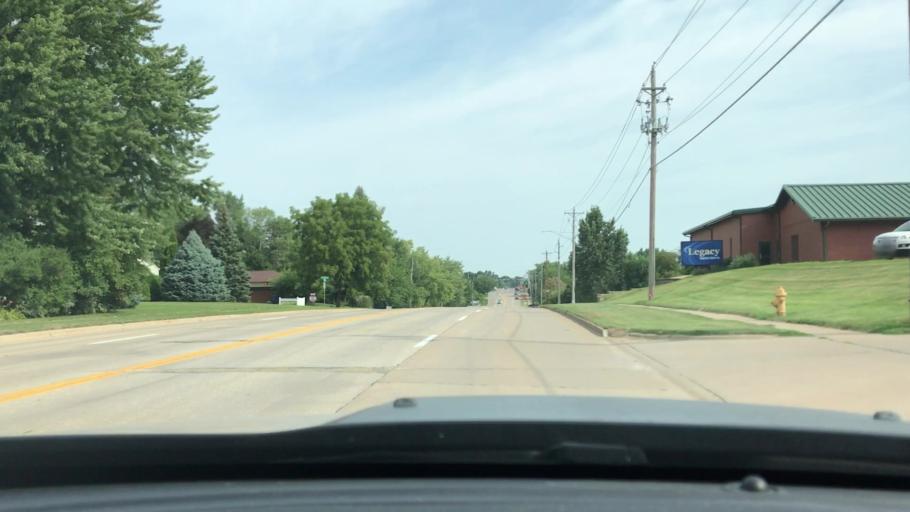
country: US
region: Iowa
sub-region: Scott County
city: Bettendorf
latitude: 41.5696
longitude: -90.5416
